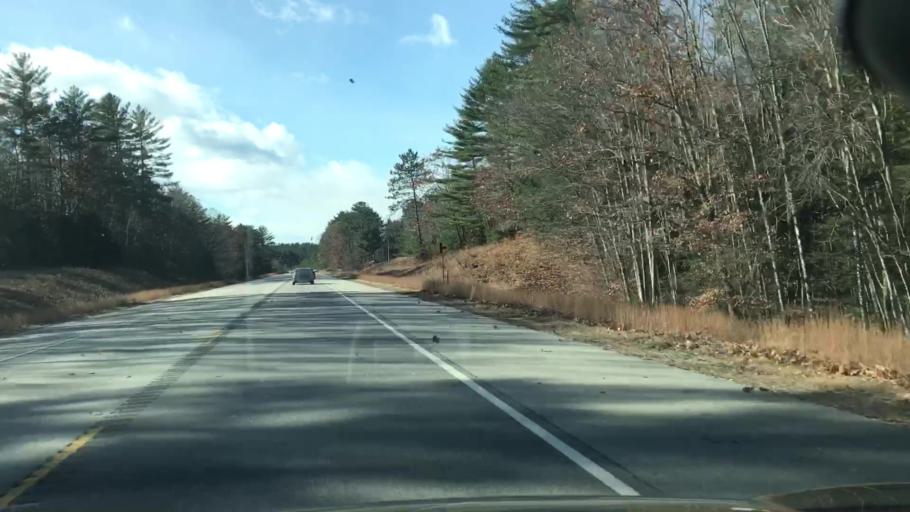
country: US
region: New Hampshire
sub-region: Belknap County
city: Barnstead
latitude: 43.3404
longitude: -71.2856
